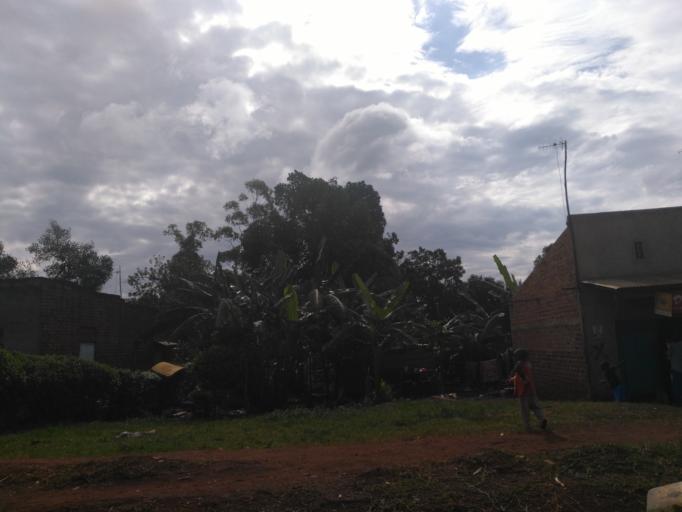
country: UG
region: Central Region
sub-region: Buikwe District
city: Njeru
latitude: 0.4049
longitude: 33.1783
